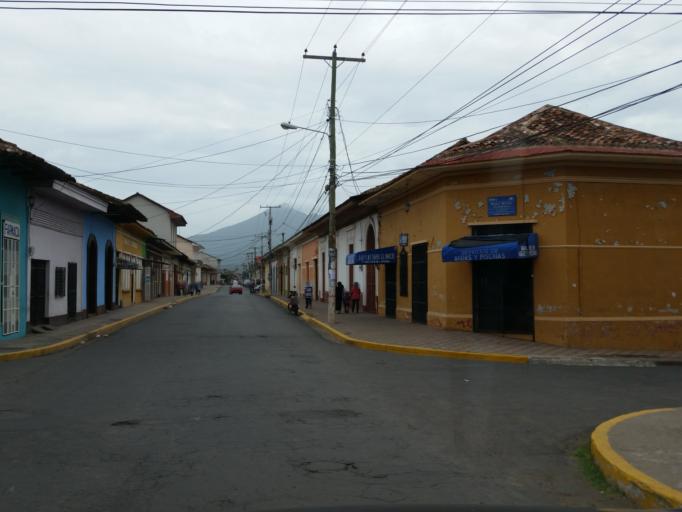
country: NI
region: Granada
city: Granada
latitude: 11.9337
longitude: -85.9553
